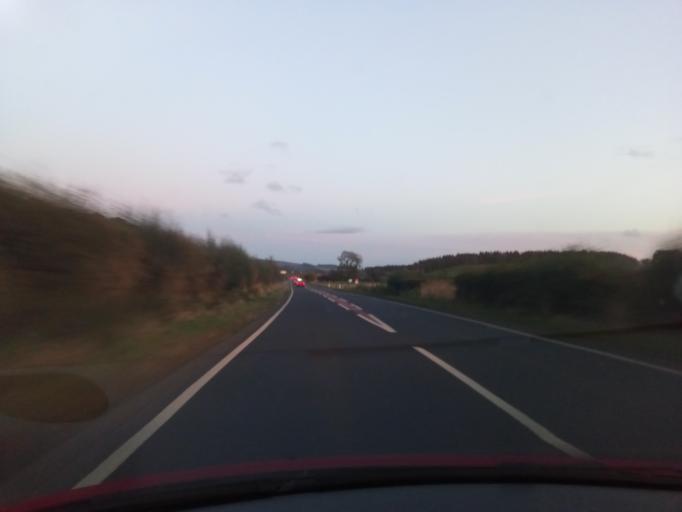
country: GB
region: Scotland
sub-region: The Scottish Borders
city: Lauder
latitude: 55.7758
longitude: -2.7980
